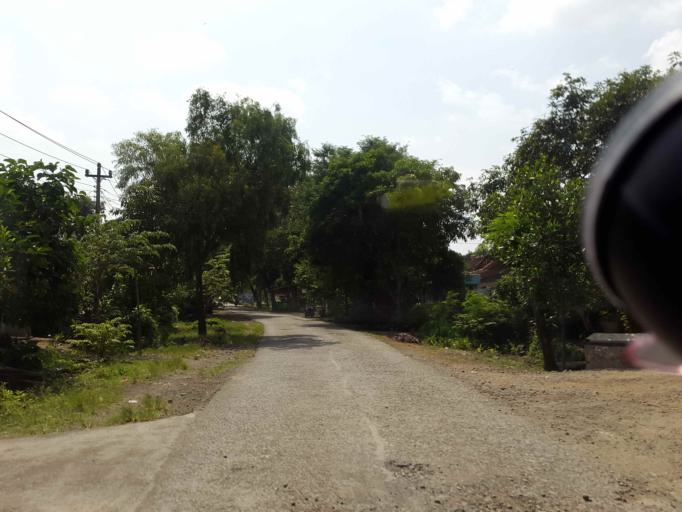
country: ID
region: Central Java
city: Pemalang
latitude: -6.9479
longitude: 109.3463
